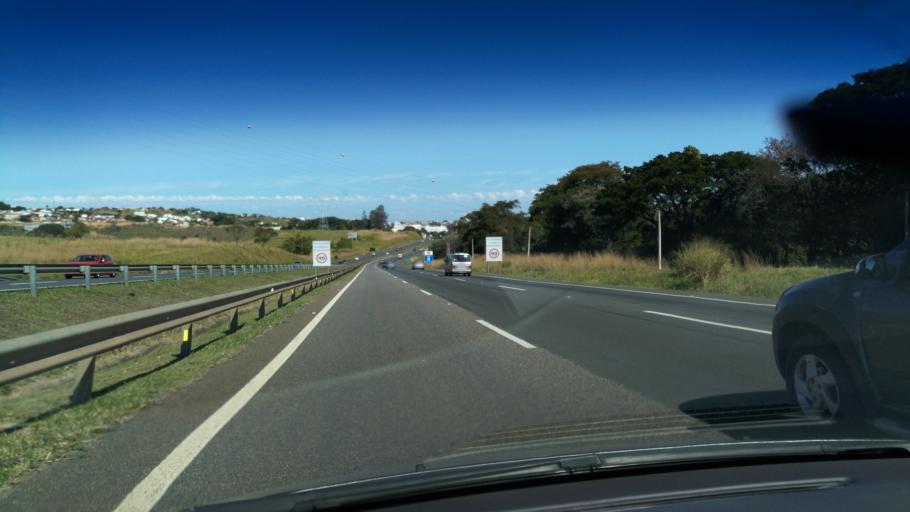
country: BR
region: Sao Paulo
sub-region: Campinas
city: Campinas
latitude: -22.8032
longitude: -47.0330
